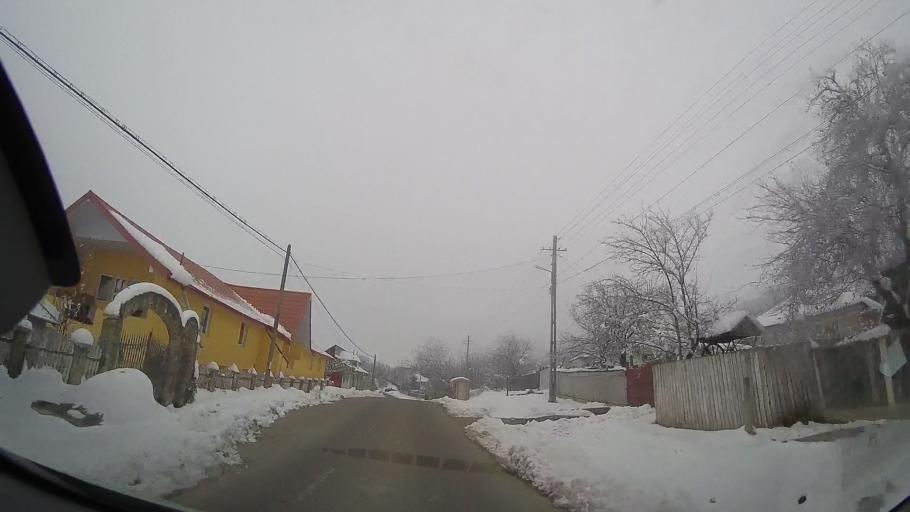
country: RO
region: Neamt
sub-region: Comuna Bozieni
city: Bozieni
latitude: 46.8413
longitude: 27.1470
